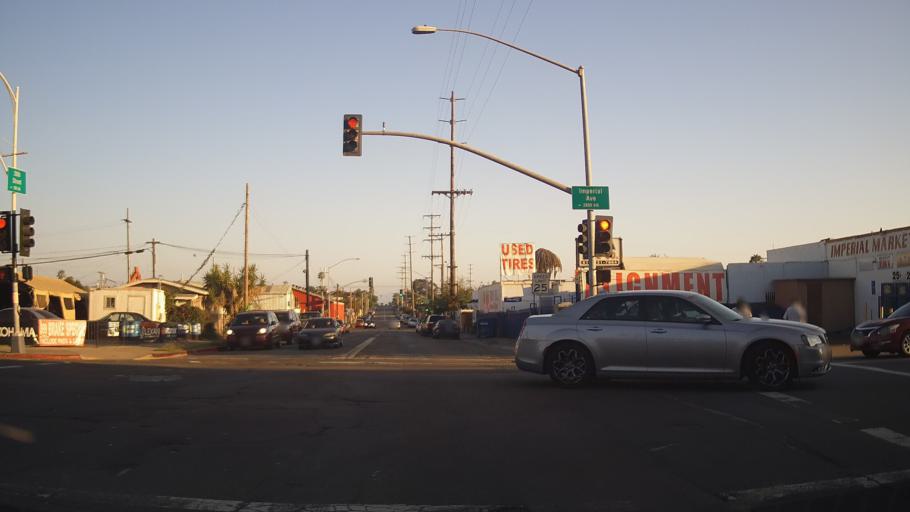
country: US
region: California
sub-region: San Diego County
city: San Diego
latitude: 32.7065
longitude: -117.1339
